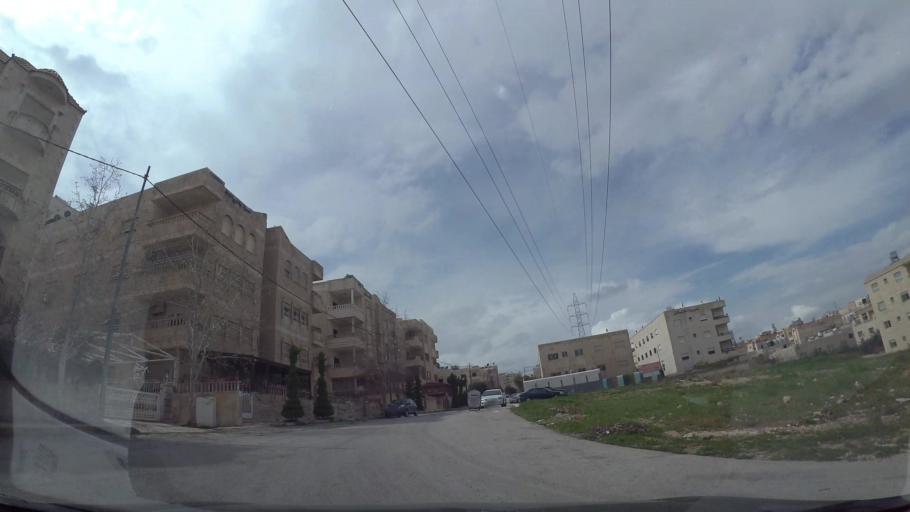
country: JO
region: Amman
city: Amman
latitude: 31.9930
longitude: 35.9424
